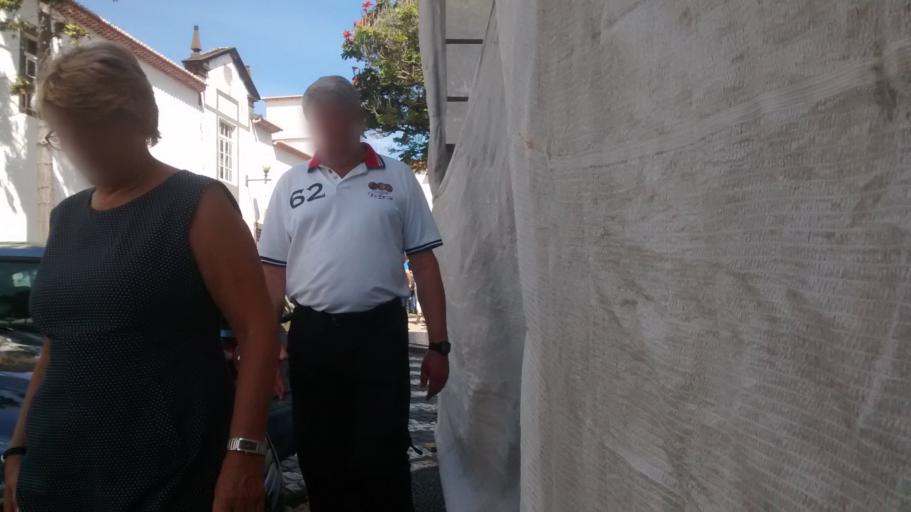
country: PT
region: Madeira
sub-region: Funchal
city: Nossa Senhora do Monte
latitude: 32.6502
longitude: -16.9091
